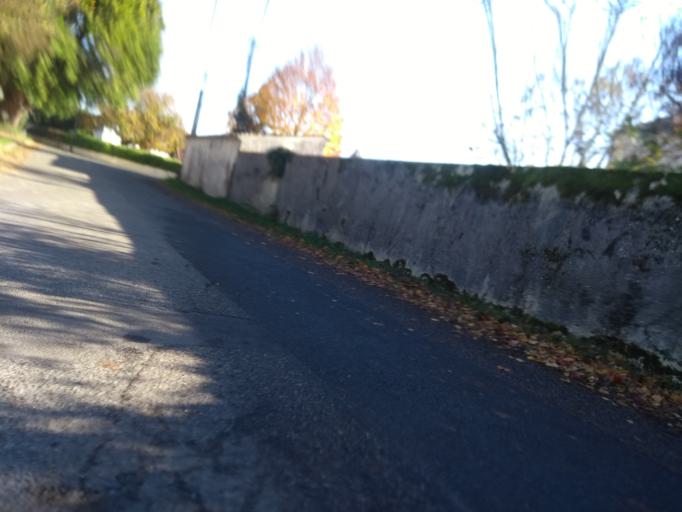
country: FR
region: Aquitaine
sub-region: Departement de la Gironde
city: Leognan
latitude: 44.7381
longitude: -0.6004
